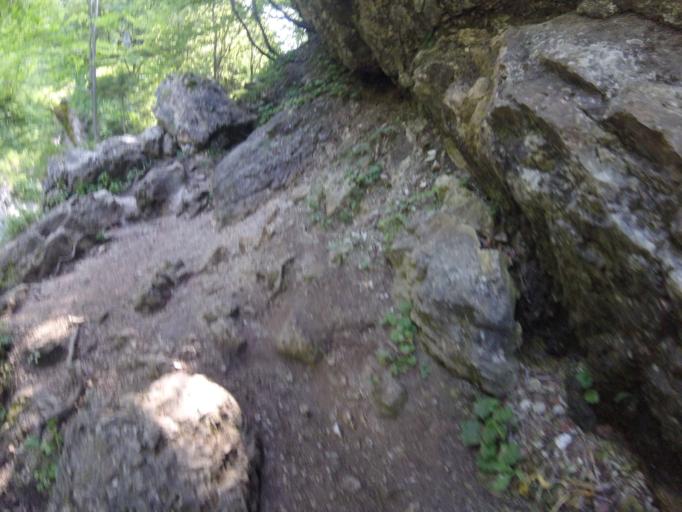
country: SK
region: Zilinsky
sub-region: Okres Zilina
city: Terchova
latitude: 49.2411
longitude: 19.0797
